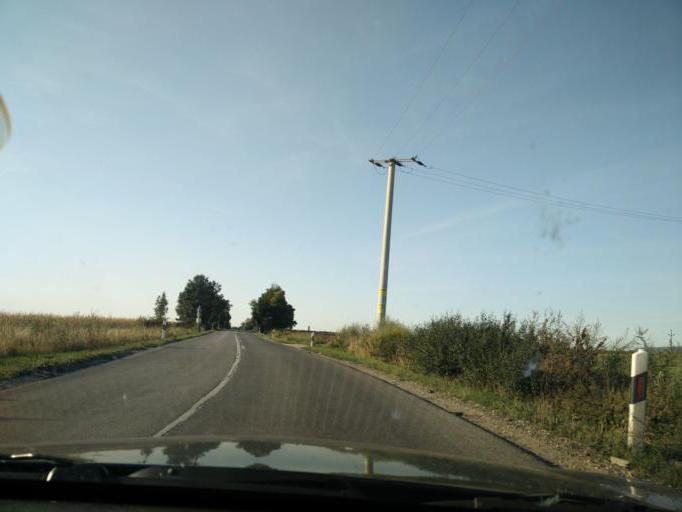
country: HU
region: Pest
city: Perbal
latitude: 47.5947
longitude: 18.7717
